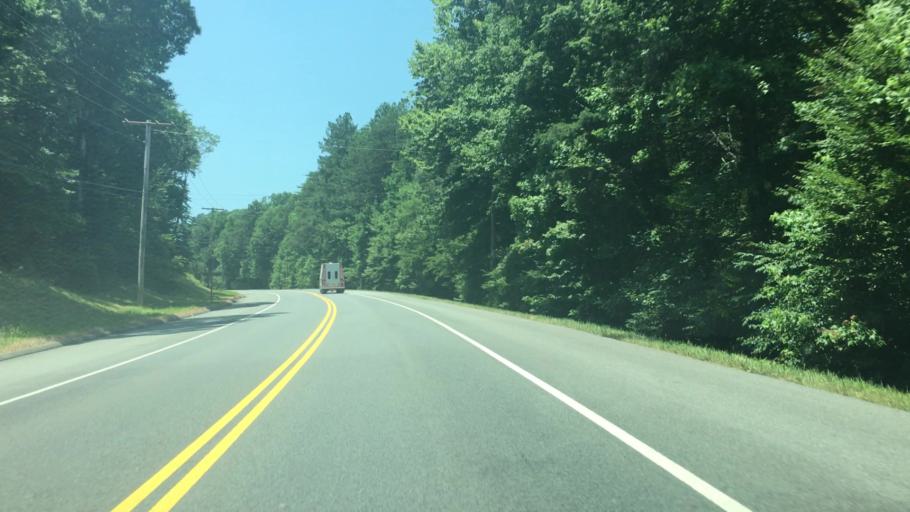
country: US
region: Maryland
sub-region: Saint Mary's County
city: Mechanicsville
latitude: 38.3734
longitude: -76.7897
